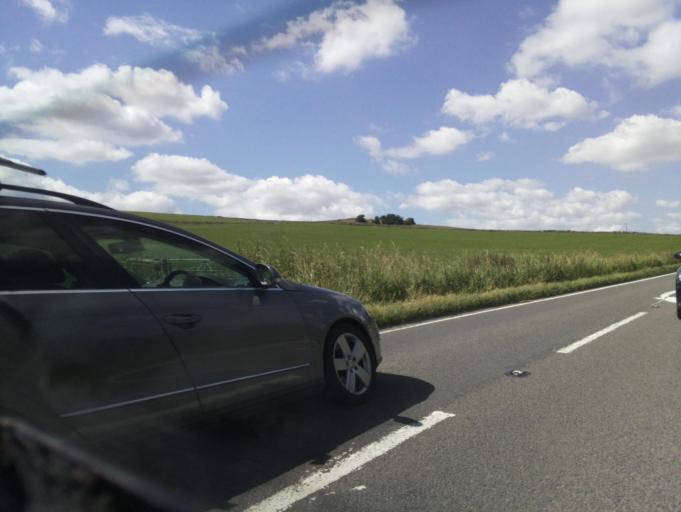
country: GB
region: England
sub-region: Derbyshire
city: Ashbourne
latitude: 53.0853
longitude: -1.7632
